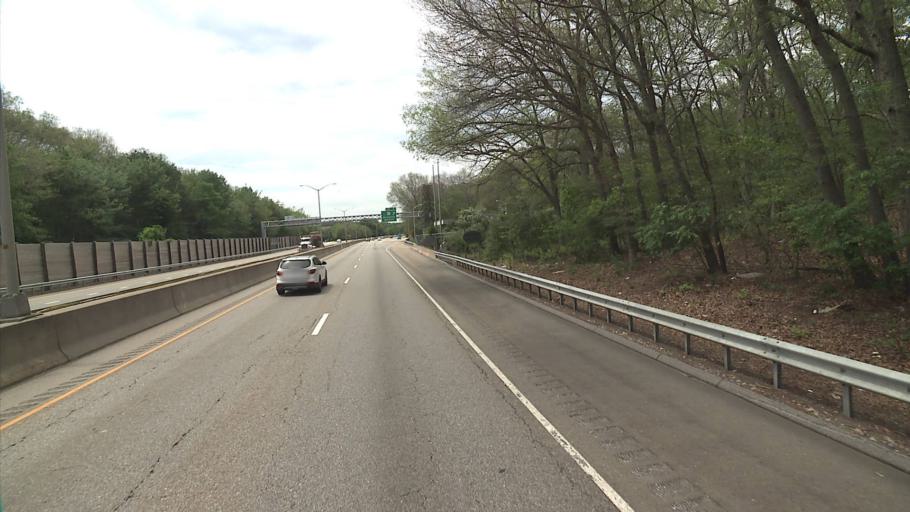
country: US
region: Connecticut
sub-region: New London County
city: Norwich
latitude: 41.4813
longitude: -72.0925
